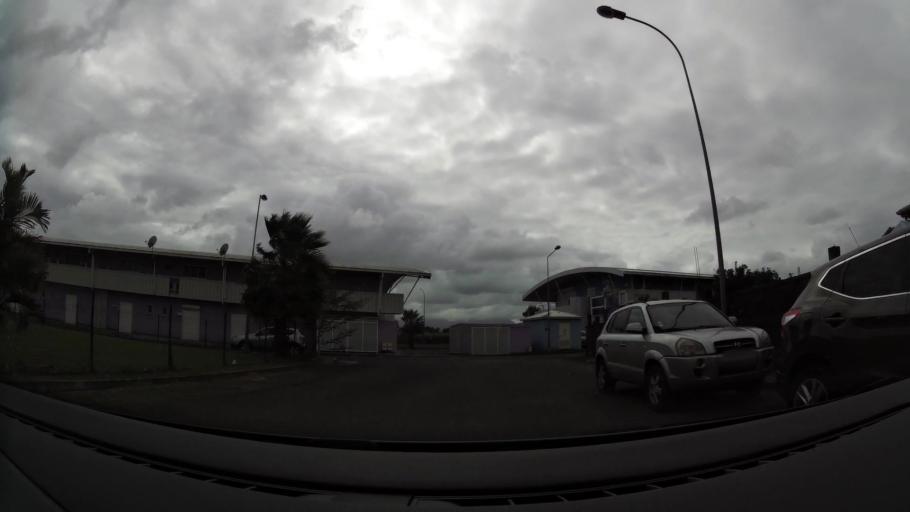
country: GP
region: Guadeloupe
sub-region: Guadeloupe
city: Lamentin
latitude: 16.2608
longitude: -61.6239
